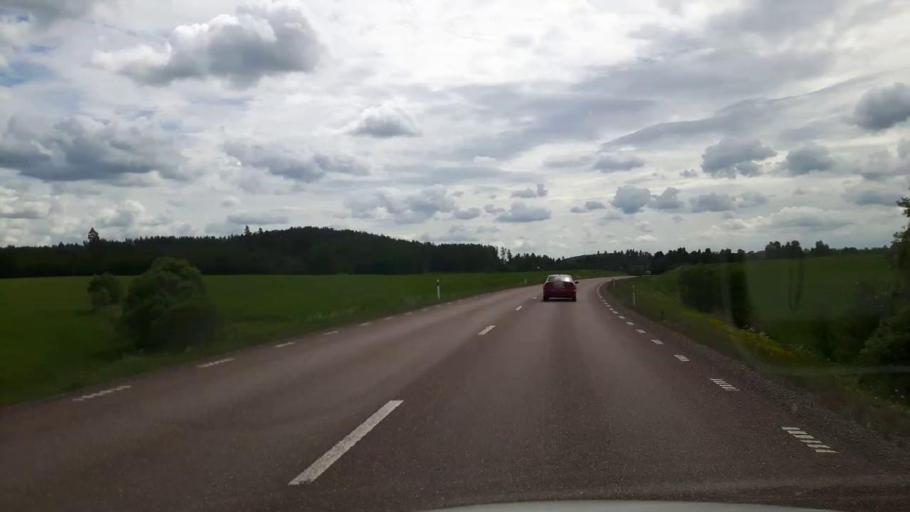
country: SE
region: Dalarna
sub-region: Hedemora Kommun
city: Hedemora
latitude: 60.3306
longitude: 15.9489
